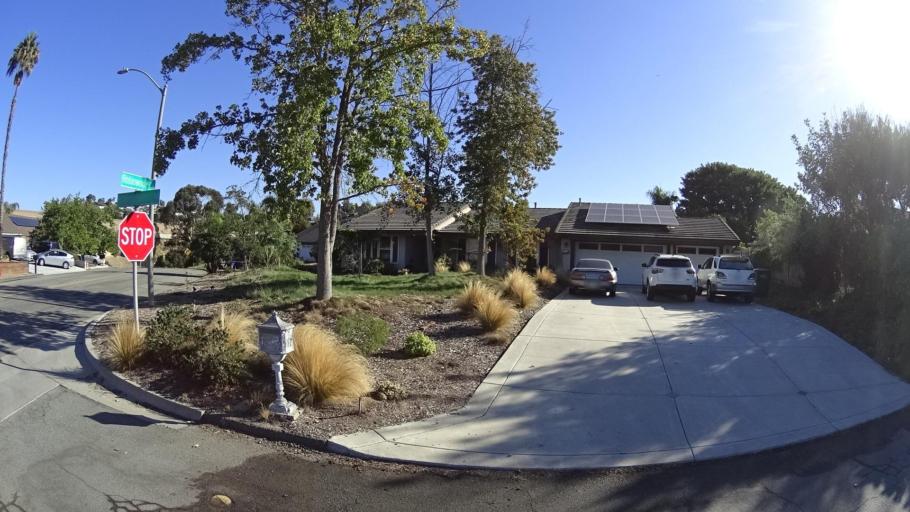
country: US
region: California
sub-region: San Diego County
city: Bonita
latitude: 32.6854
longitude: -117.0228
